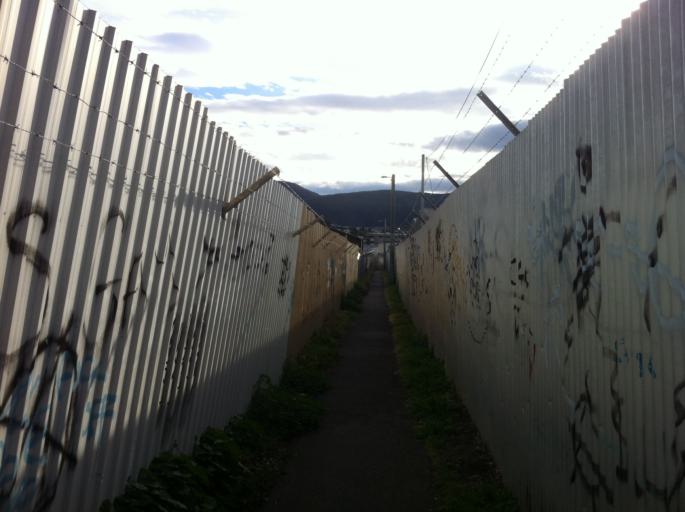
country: AU
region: Tasmania
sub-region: Glenorchy
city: Moonah
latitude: -42.8427
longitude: 147.2981
